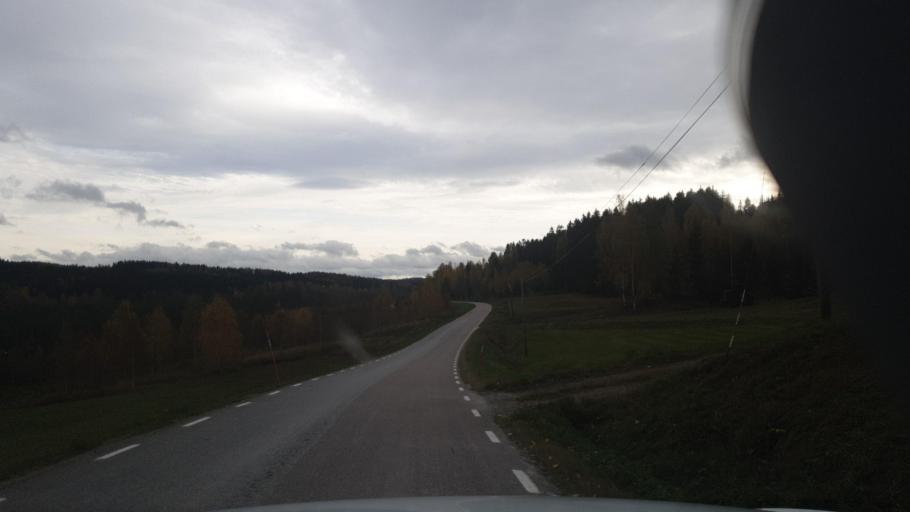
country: SE
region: Vaermland
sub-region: Arvika Kommun
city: Arvika
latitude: 59.7840
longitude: 12.7673
